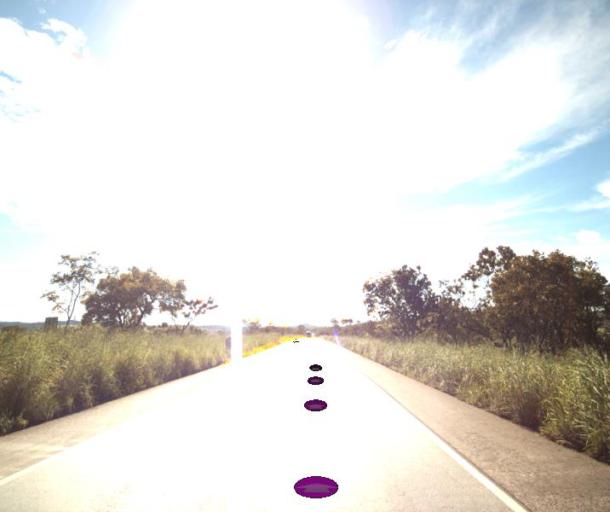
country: BR
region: Goias
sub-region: Jaragua
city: Jaragua
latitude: -15.5374
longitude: -49.4426
